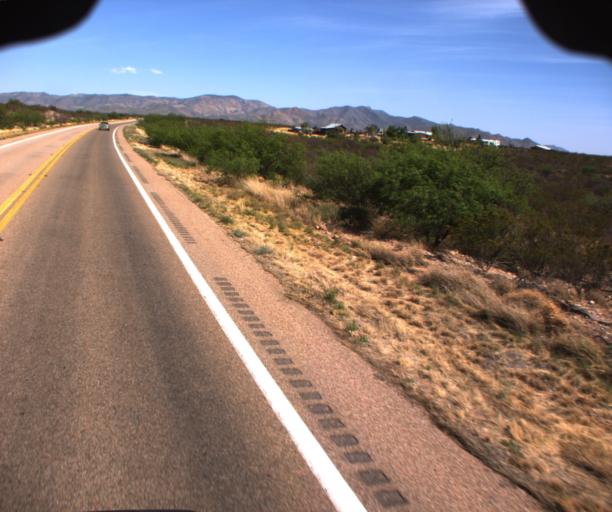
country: US
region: Arizona
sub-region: Cochise County
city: Sierra Vista Southeast
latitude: 31.5487
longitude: -110.1039
